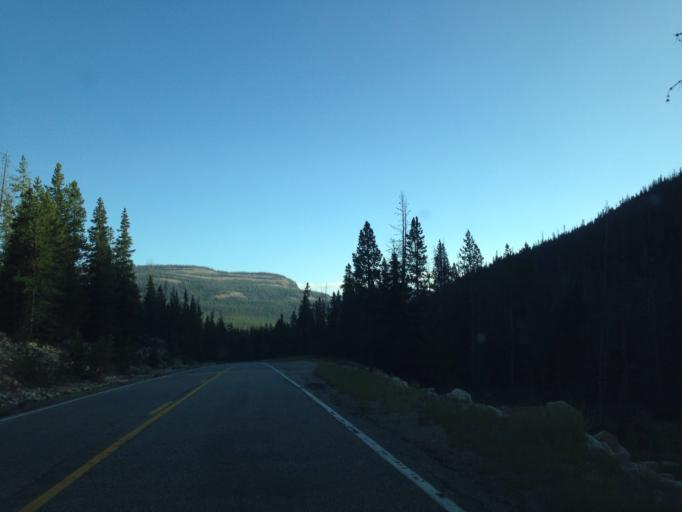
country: US
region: Utah
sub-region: Summit County
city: Kamas
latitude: 40.6523
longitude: -110.9450
